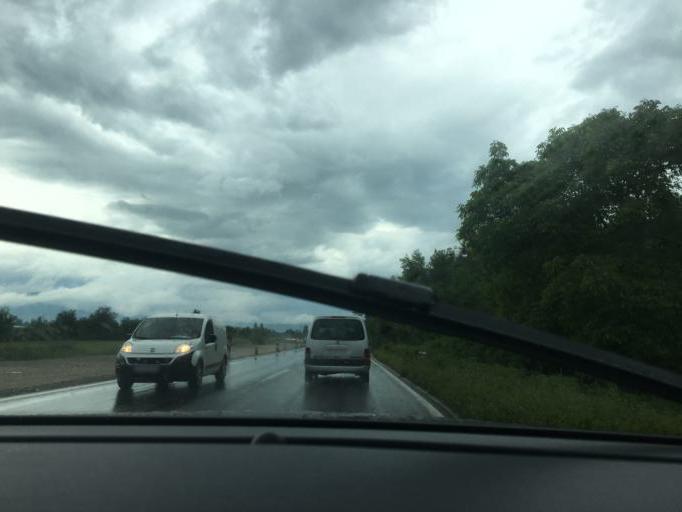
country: MK
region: Ohrid
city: Ohrid
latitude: 41.1528
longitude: 20.7568
